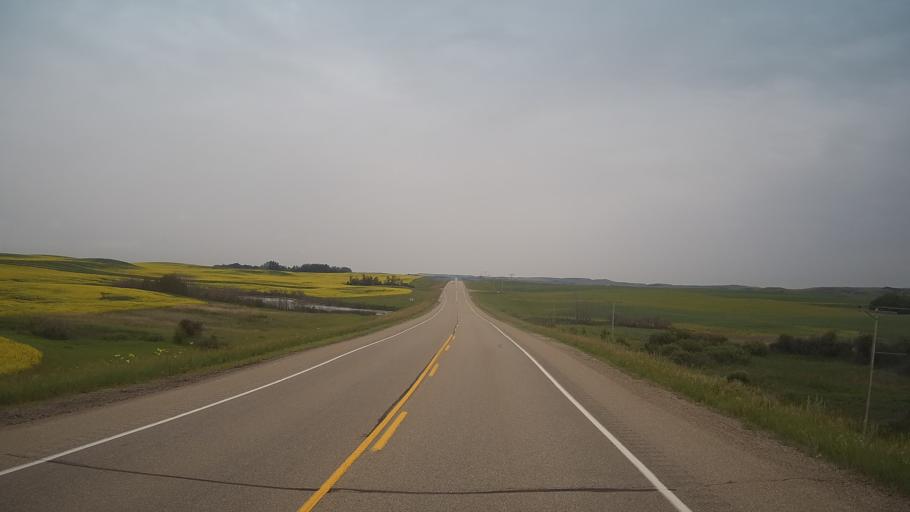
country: CA
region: Saskatchewan
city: Biggar
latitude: 52.0566
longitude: -107.7818
